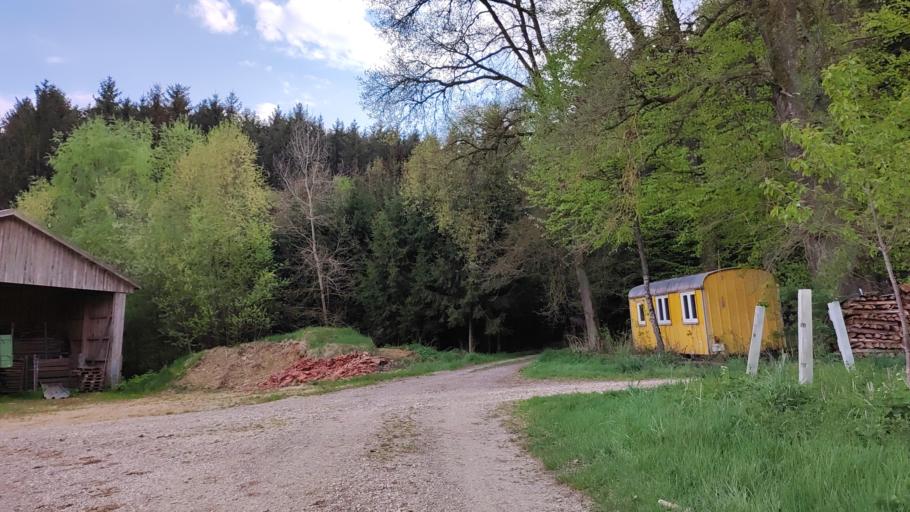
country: DE
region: Bavaria
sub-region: Swabia
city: Zusmarshausen
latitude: 48.3949
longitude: 10.5737
